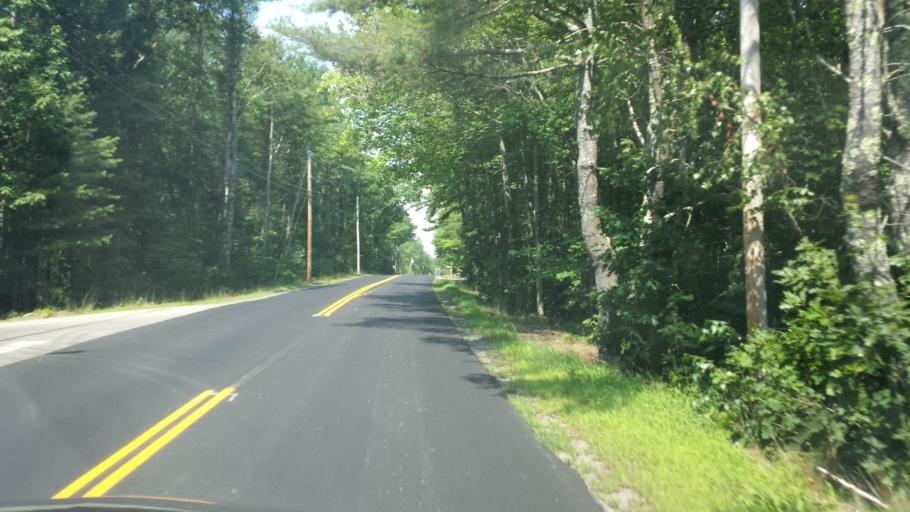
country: US
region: Maine
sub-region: York County
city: Biddeford
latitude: 43.4447
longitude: -70.4129
